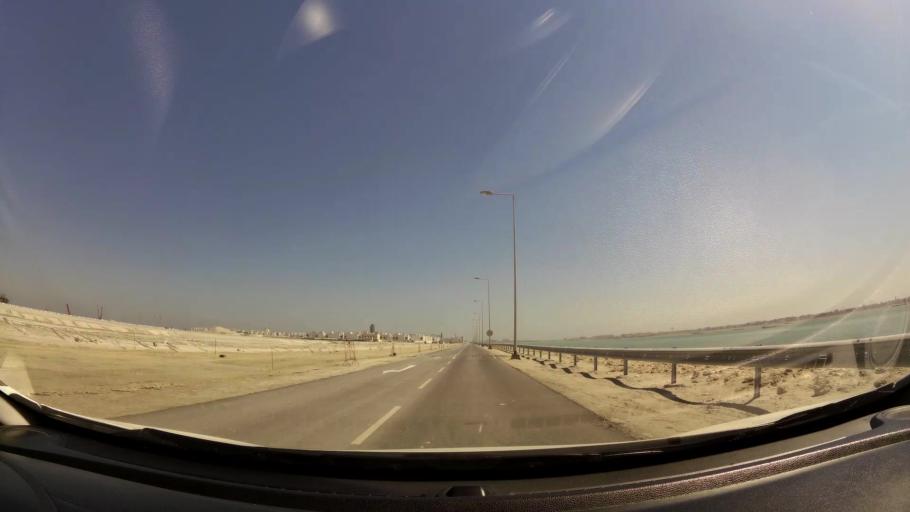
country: BH
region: Muharraq
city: Al Muharraq
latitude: 26.3030
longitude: 50.6273
